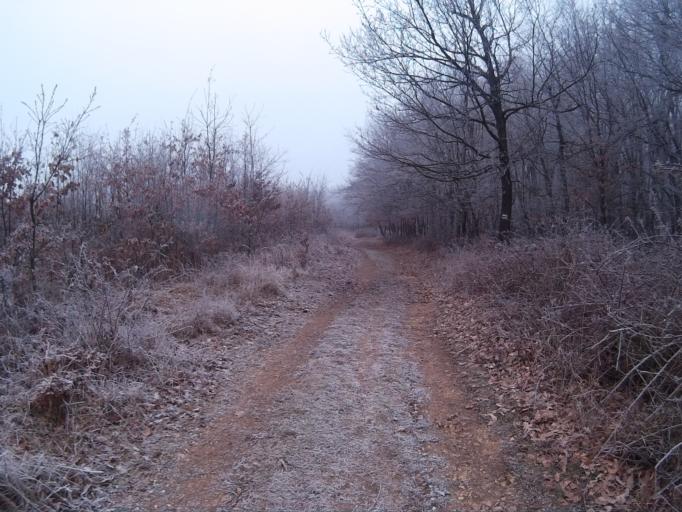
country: HU
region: Komarom-Esztergom
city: Oroszlany
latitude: 47.4426
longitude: 18.3691
